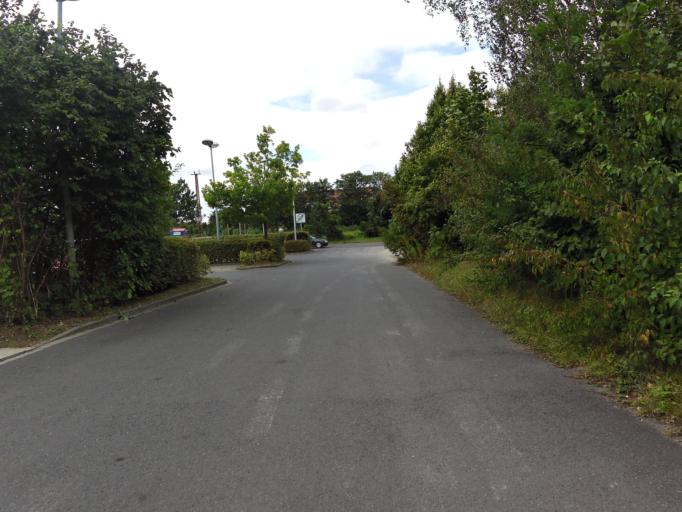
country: DE
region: Saxony
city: Rackwitz
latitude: 51.3887
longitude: 12.3697
